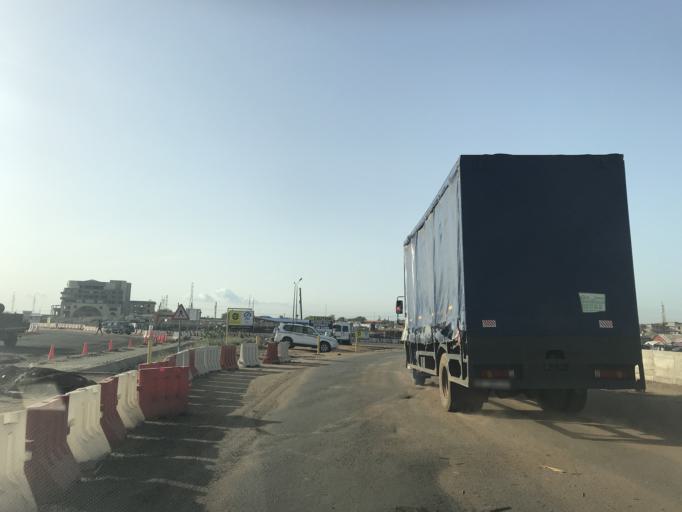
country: GH
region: Greater Accra
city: Tema
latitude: 5.6838
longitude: -0.0139
